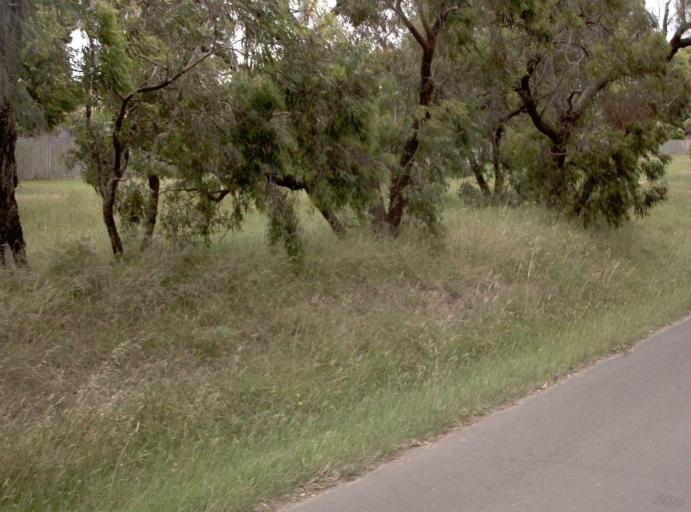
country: AU
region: Victoria
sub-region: Casey
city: Cranbourne North
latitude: -38.0718
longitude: 145.2700
